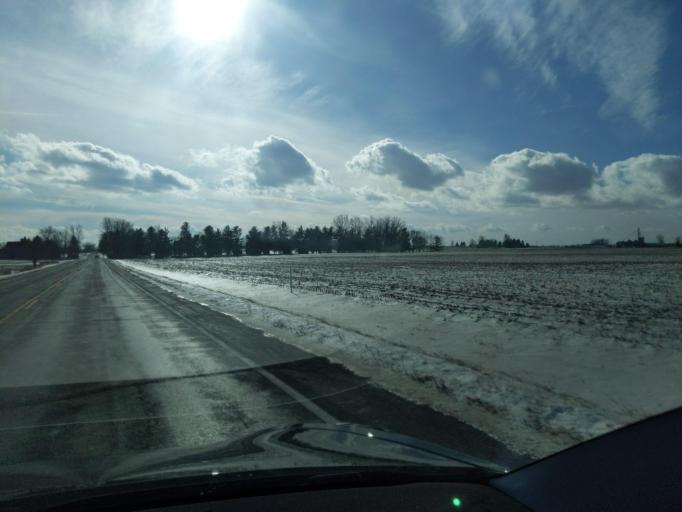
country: US
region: Michigan
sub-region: Ingham County
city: Williamston
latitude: 42.6064
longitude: -84.2795
